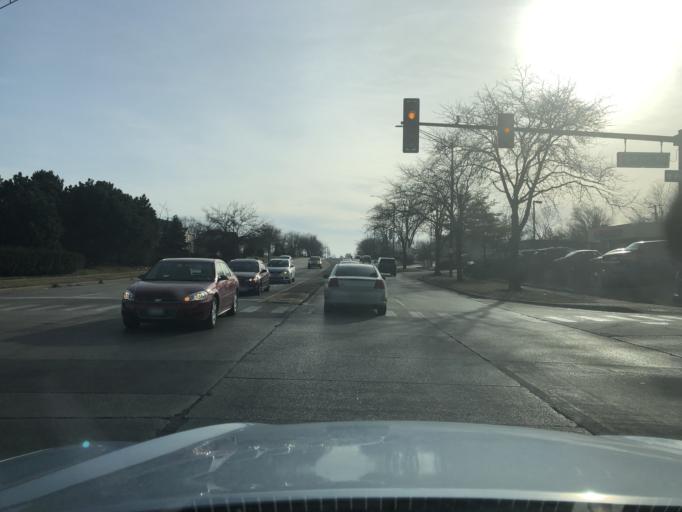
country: US
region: Illinois
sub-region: DuPage County
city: Roselle
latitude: 42.0054
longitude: -88.0802
